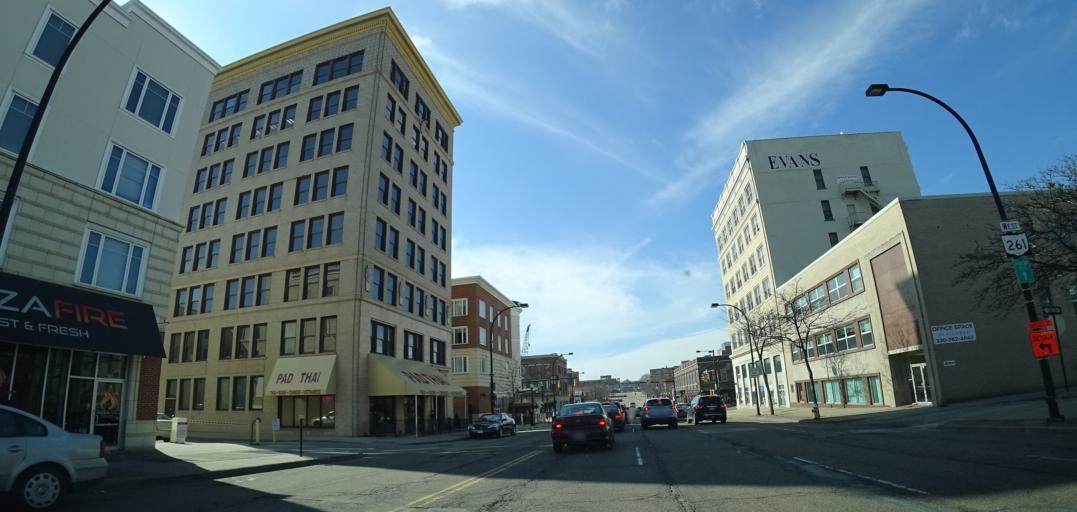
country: US
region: Ohio
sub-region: Summit County
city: Akron
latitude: 41.0763
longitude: -81.5212
